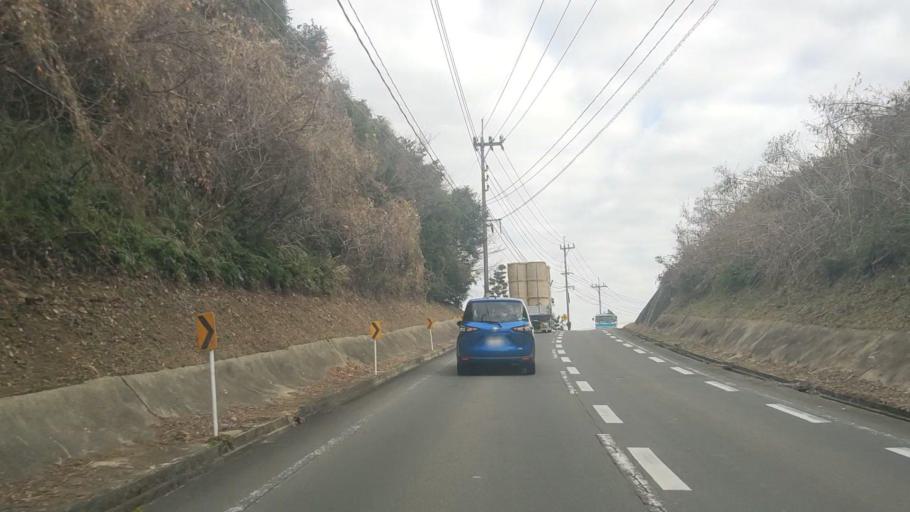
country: JP
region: Nagasaki
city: Shimabara
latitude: 32.8463
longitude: 130.2162
